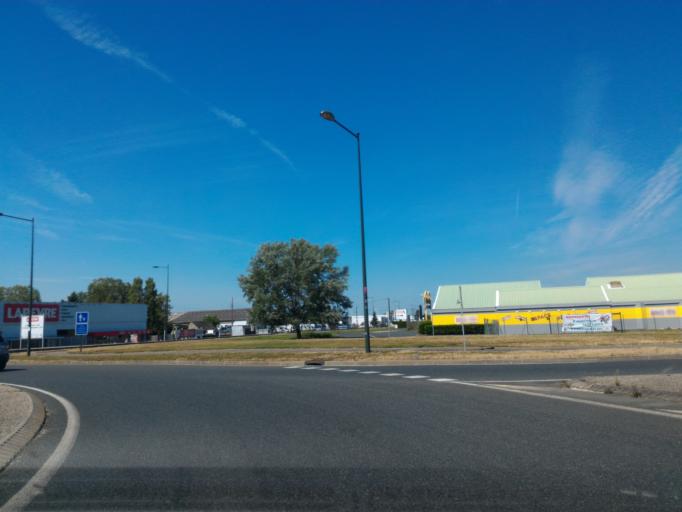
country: FR
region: Centre
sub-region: Departement de l'Indre
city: Saint-Maur
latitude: 46.7886
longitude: 1.6608
